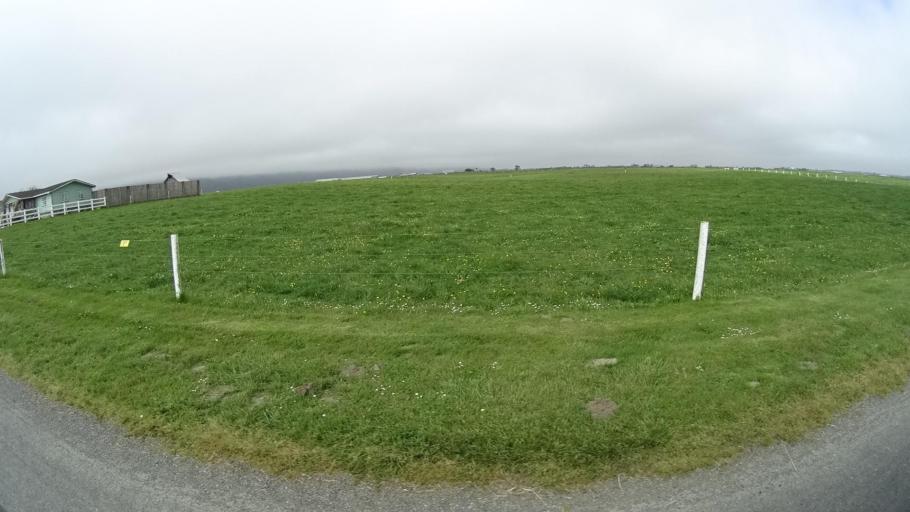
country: US
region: California
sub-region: Humboldt County
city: Fortuna
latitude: 40.5802
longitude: -124.1878
